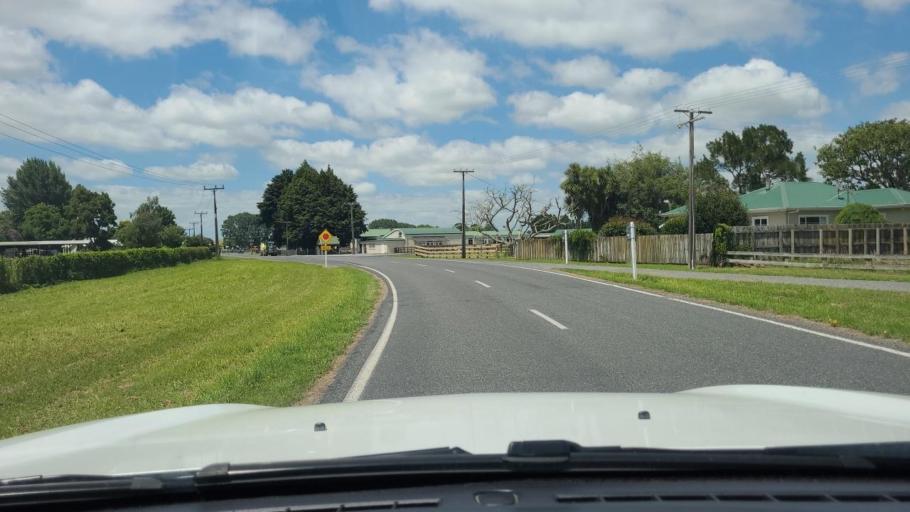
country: NZ
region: Waikato
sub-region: Matamata-Piako District
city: Matamata
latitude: -37.8790
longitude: 175.7585
